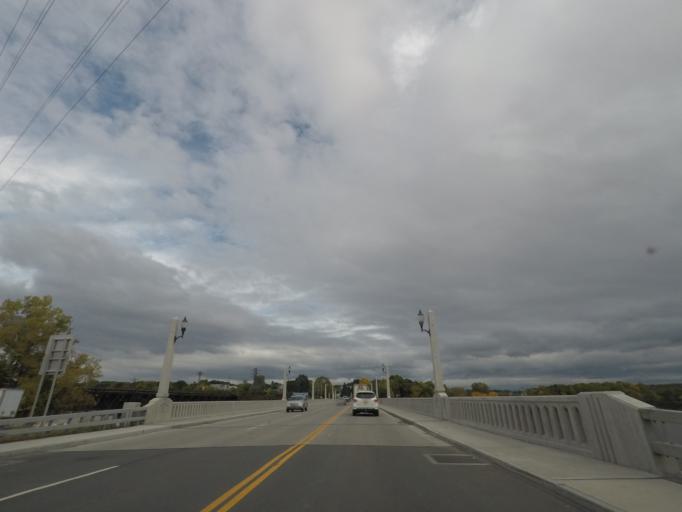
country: US
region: New York
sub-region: Albany County
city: Cohoes
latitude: 42.7771
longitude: -73.6967
